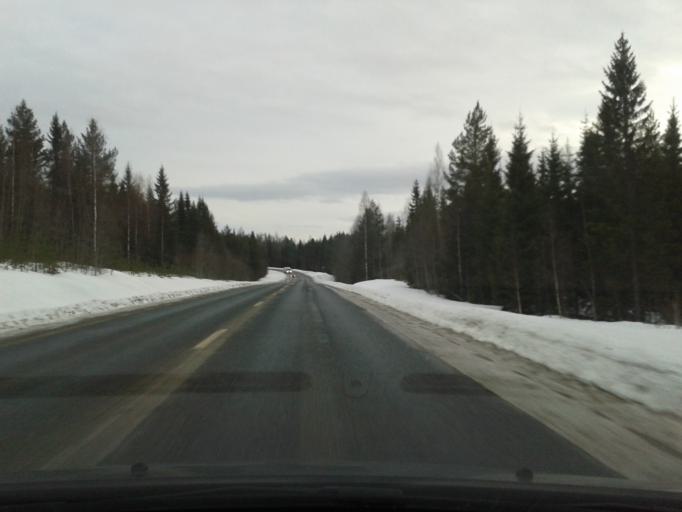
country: SE
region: Vaesternorrland
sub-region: Solleftea Kommun
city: Solleftea
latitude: 63.4035
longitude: 16.9722
